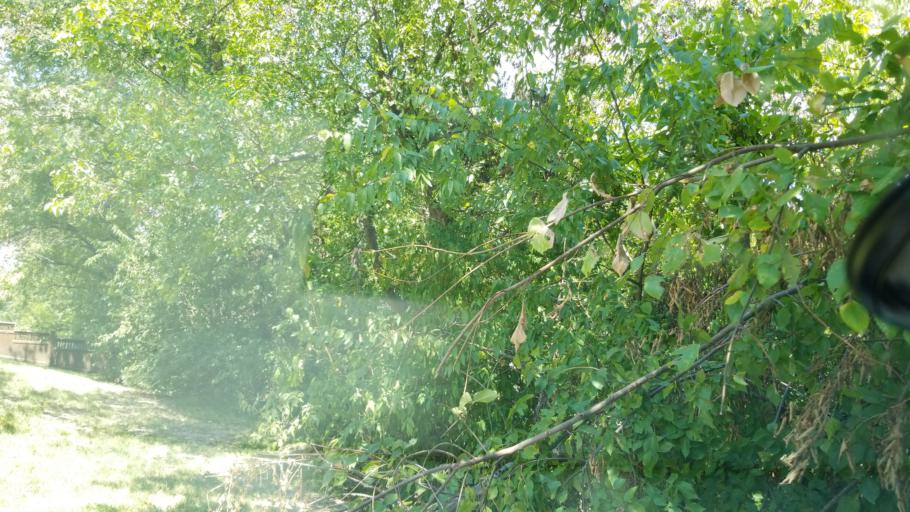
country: US
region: Texas
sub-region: Dallas County
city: Richardson
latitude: 32.8852
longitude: -96.7120
